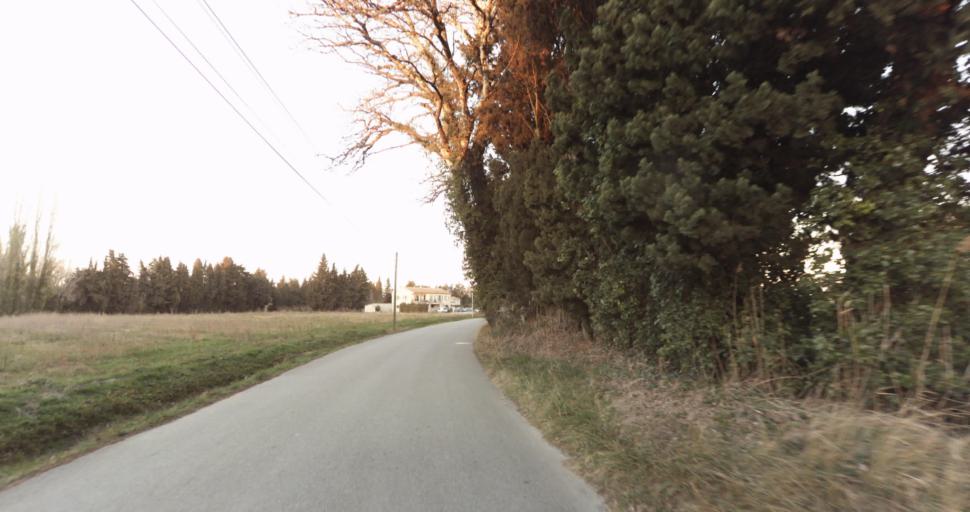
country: FR
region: Provence-Alpes-Cote d'Azur
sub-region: Departement des Bouches-du-Rhone
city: Barbentane
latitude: 43.9071
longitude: 4.7609
